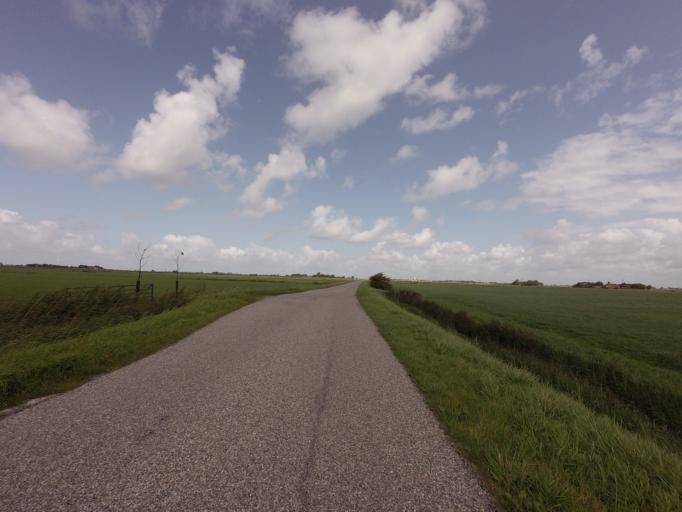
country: NL
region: Friesland
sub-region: Gemeente Franekeradeel
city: Sexbierum
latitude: 53.1622
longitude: 5.4844
